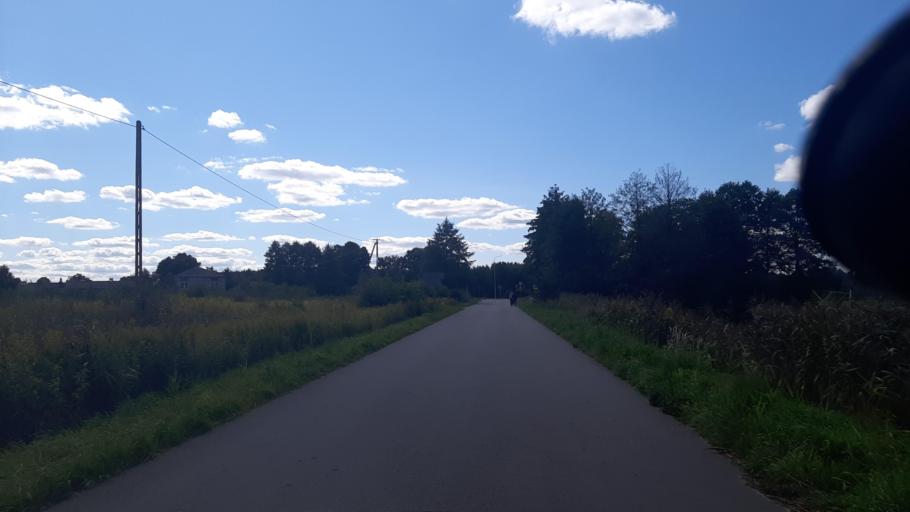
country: PL
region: Lublin Voivodeship
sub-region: Powiat lubelski
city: Garbow
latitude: 51.4041
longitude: 22.3578
